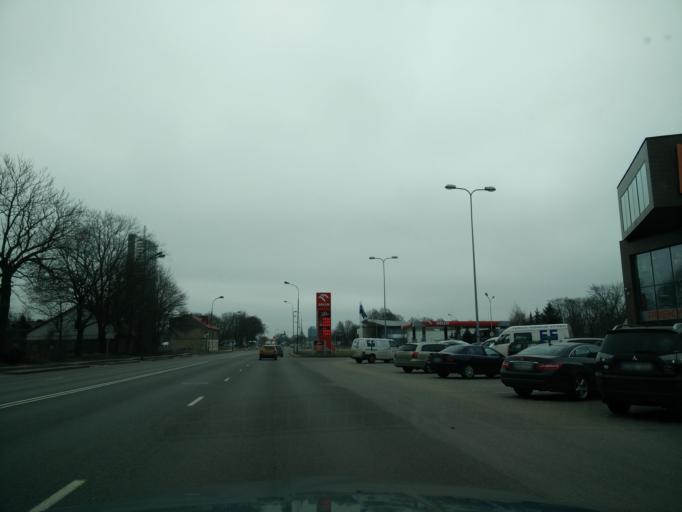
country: LT
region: Klaipedos apskritis
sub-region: Klaipeda
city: Klaipeda
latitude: 55.6949
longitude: 21.1399
